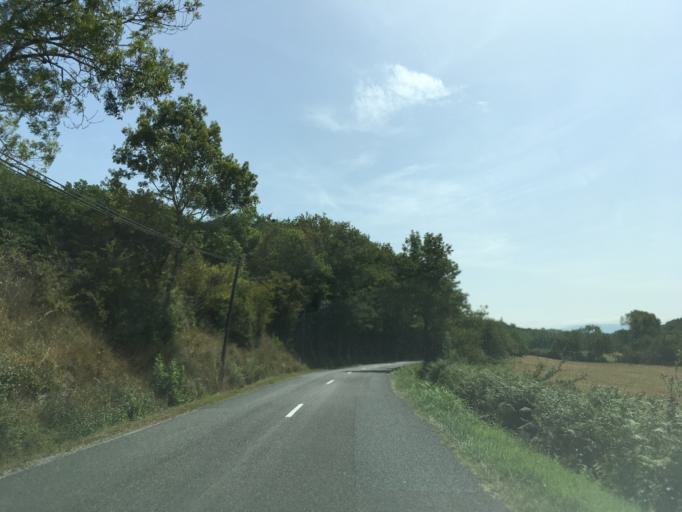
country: FR
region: Midi-Pyrenees
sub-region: Departement du Tarn
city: Burlats
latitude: 43.6169
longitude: 2.2974
